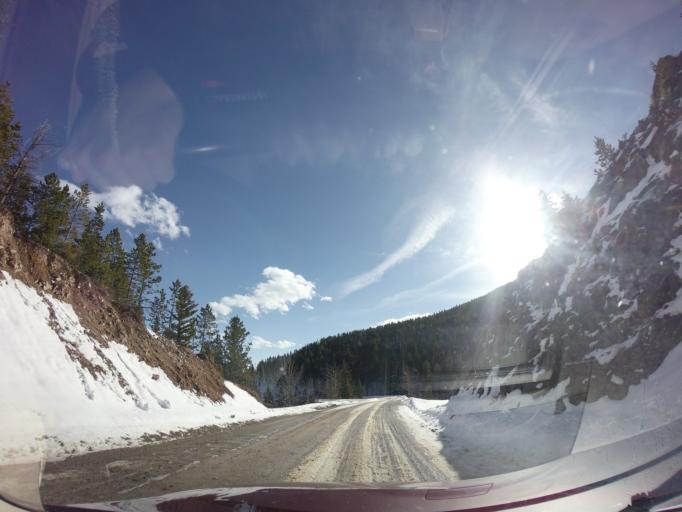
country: US
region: Montana
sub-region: Carbon County
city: Red Lodge
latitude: 45.1800
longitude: -109.3211
